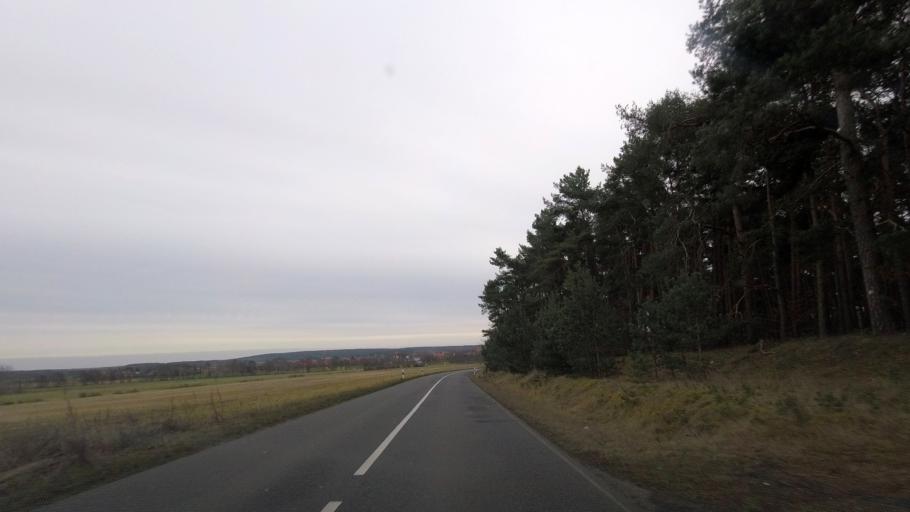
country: DE
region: Brandenburg
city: Treuenbrietzen
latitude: 52.0749
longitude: 12.9307
